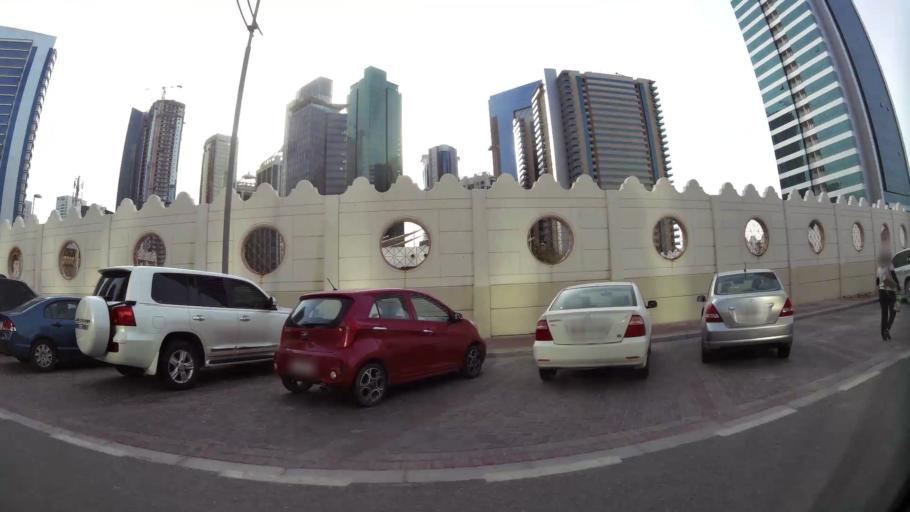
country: QA
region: Baladiyat ad Dawhah
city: Doha
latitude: 25.3292
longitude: 51.5287
